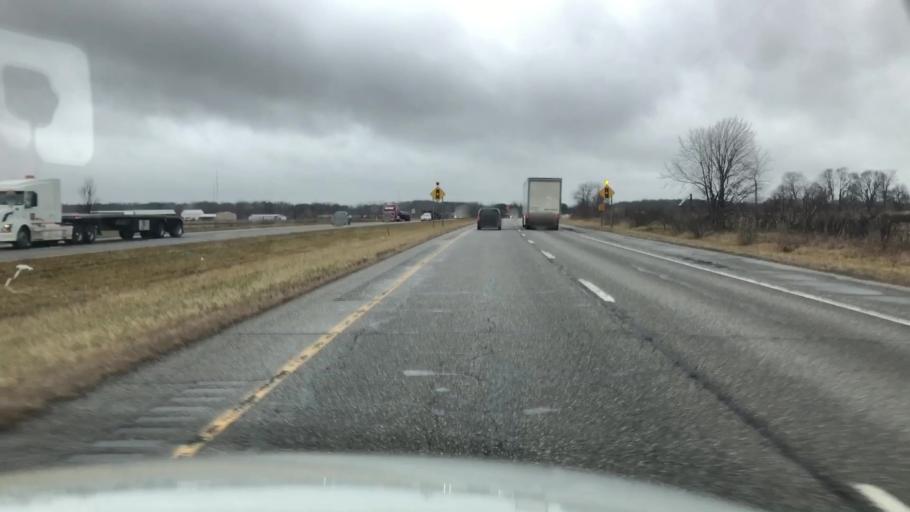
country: US
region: Indiana
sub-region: Marshall County
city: Plymouth
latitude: 41.3371
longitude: -86.2541
